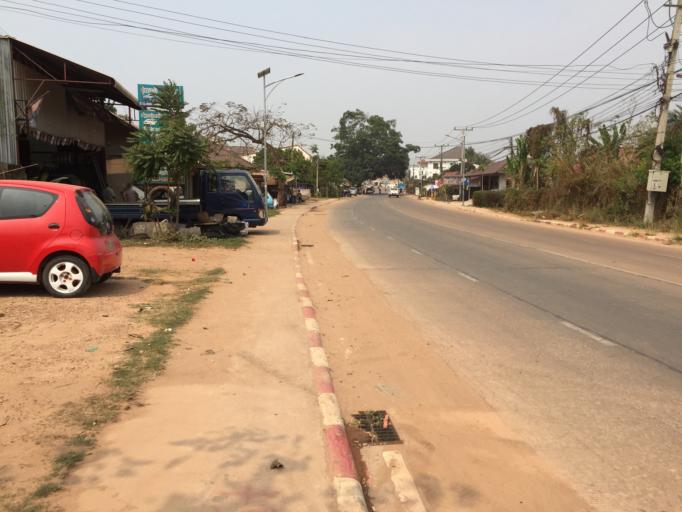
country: LA
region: Vientiane
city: Vientiane
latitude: 17.9634
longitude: 102.6701
